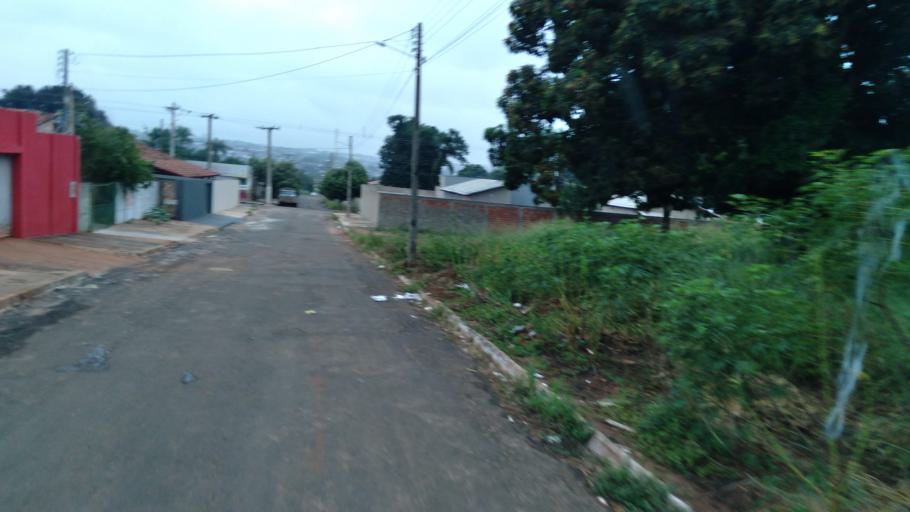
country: BR
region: Goias
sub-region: Mineiros
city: Mineiros
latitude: -17.5799
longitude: -52.5448
